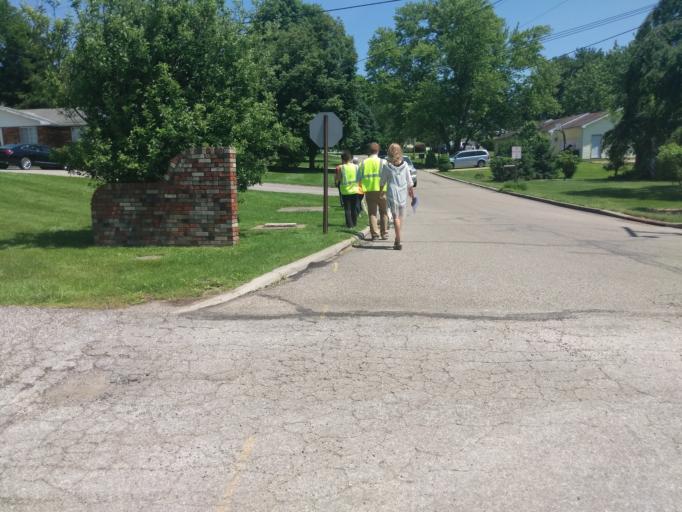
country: US
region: Ohio
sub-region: Washington County
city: Reno
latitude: 39.3944
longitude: -81.3998
